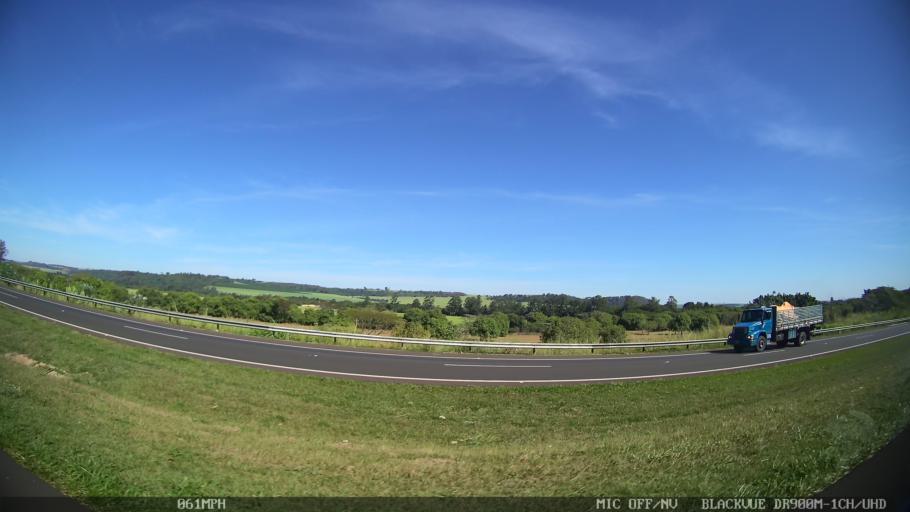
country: BR
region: Sao Paulo
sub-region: Santa Rita Do Passa Quatro
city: Santa Rita do Passa Quatro
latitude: -21.7450
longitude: -47.5759
